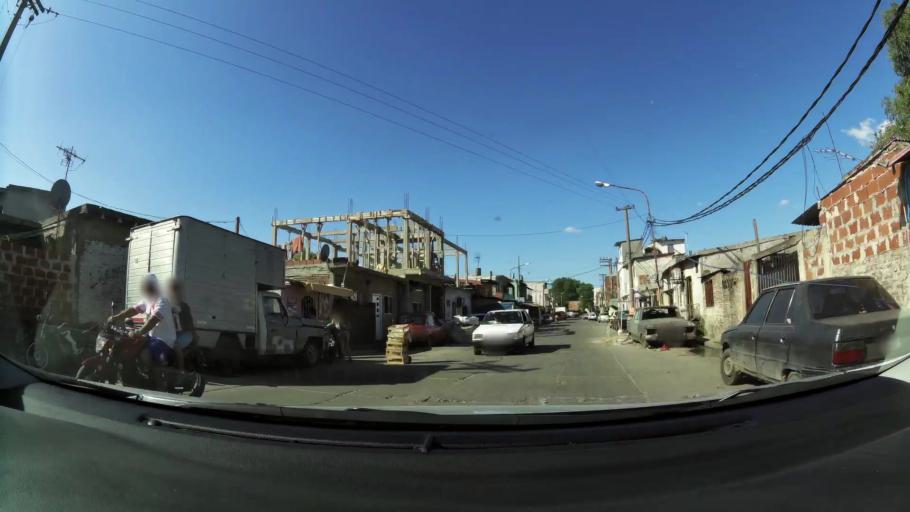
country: AR
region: Buenos Aires F.D.
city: Villa Lugano
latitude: -34.7076
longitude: -58.4891
